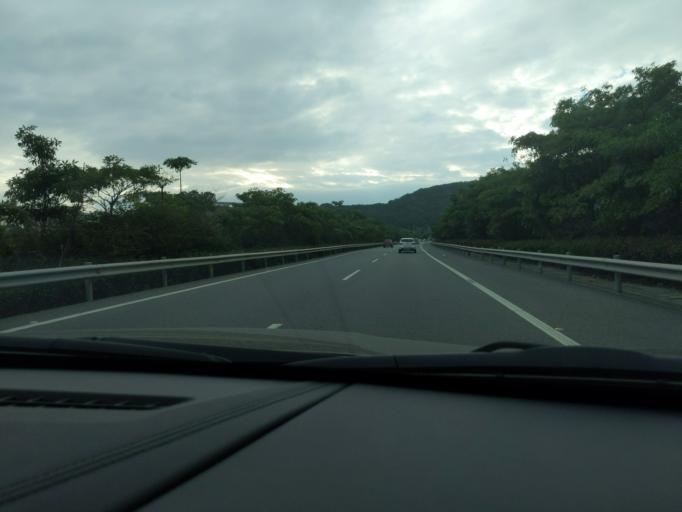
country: CN
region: Fujian
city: Dongshi
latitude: 24.7044
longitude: 118.3844
